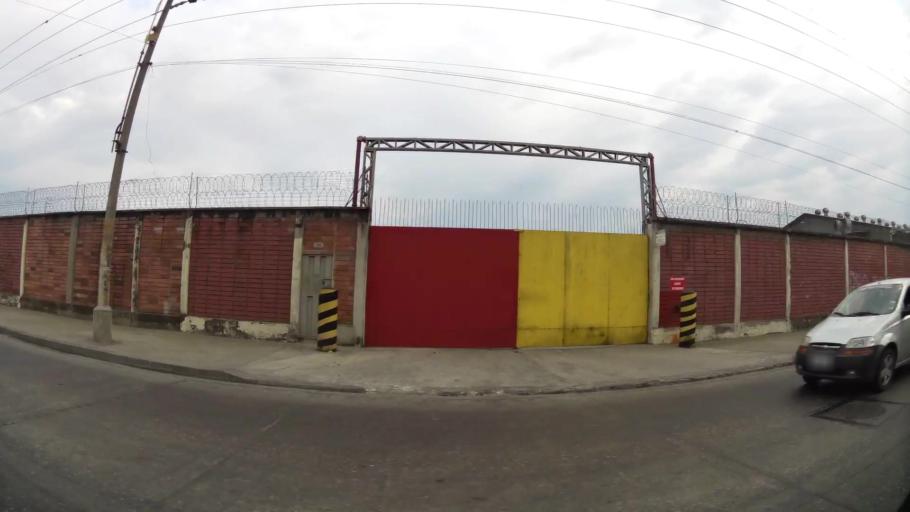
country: EC
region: Guayas
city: Guayaquil
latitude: -2.2418
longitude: -79.8857
